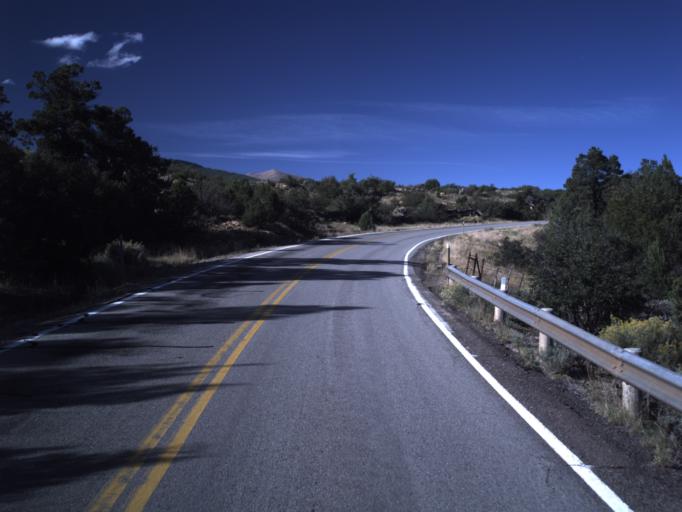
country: US
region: Utah
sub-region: Grand County
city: Moab
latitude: 38.3176
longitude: -109.2273
